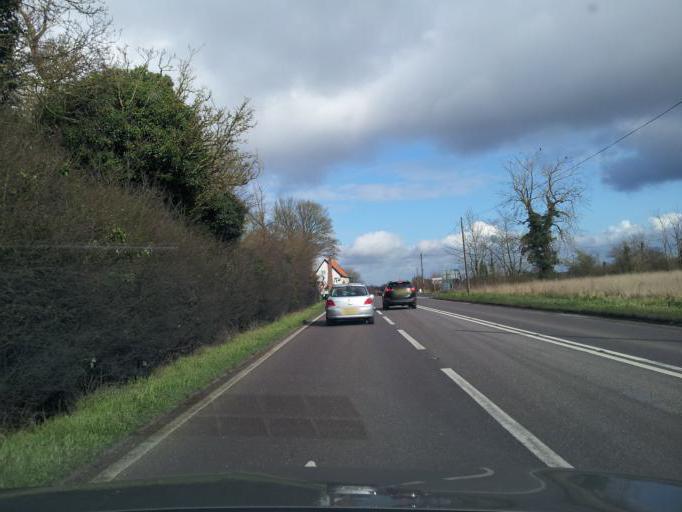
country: GB
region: England
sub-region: Norfolk
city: Diss
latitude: 52.3085
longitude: 1.1014
